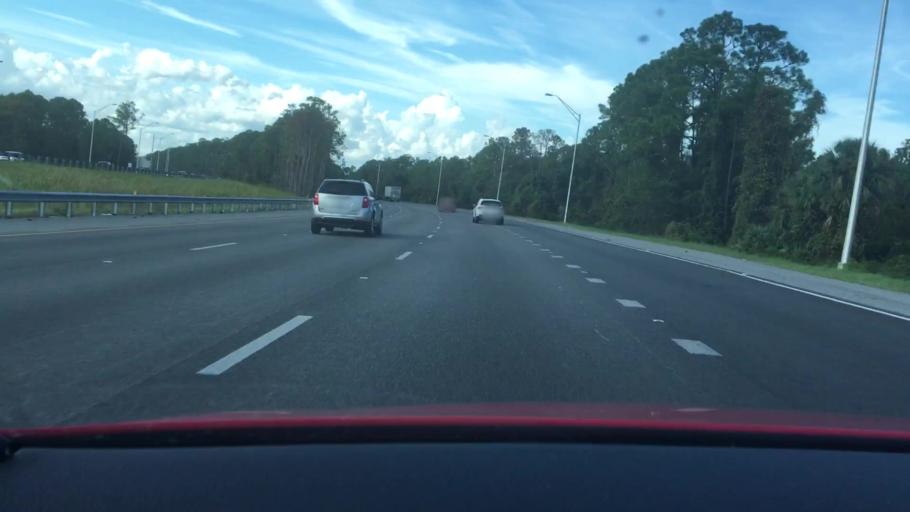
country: US
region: Florida
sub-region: Volusia County
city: Port Orange
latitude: 29.1119
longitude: -81.0316
